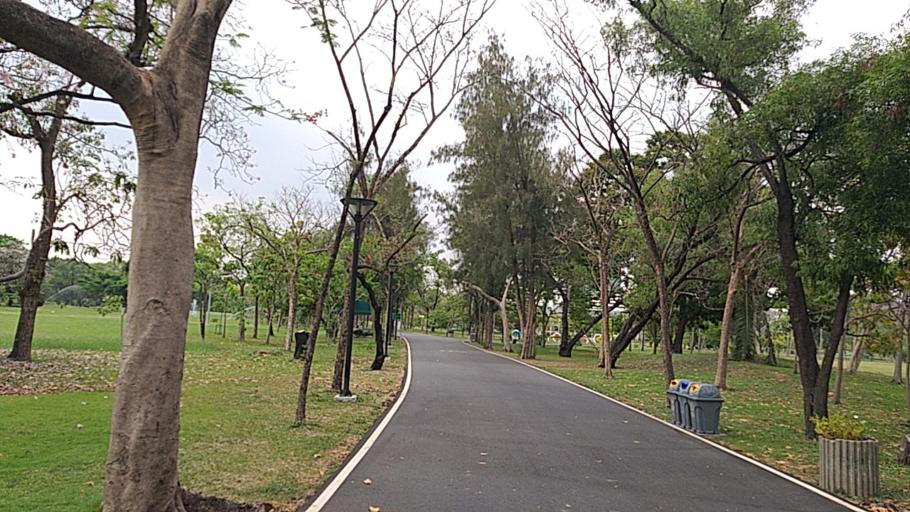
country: TH
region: Bangkok
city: Chatuchak
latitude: 13.8132
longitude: 100.5551
